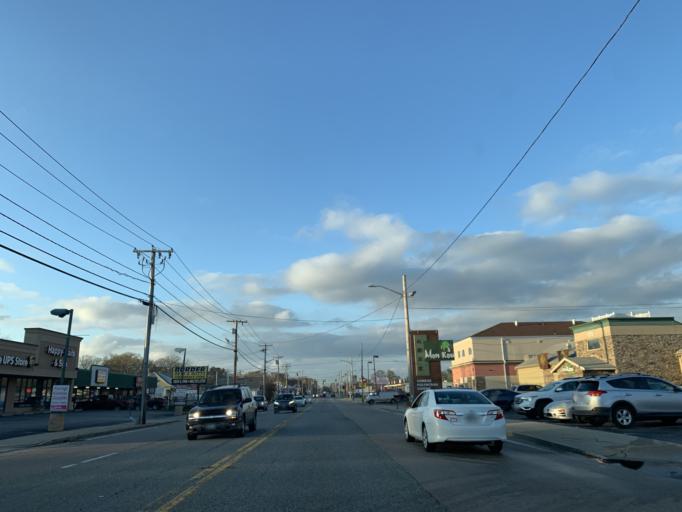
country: US
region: Rhode Island
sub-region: Providence County
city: Valley Falls
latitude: 41.9089
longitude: -71.3639
